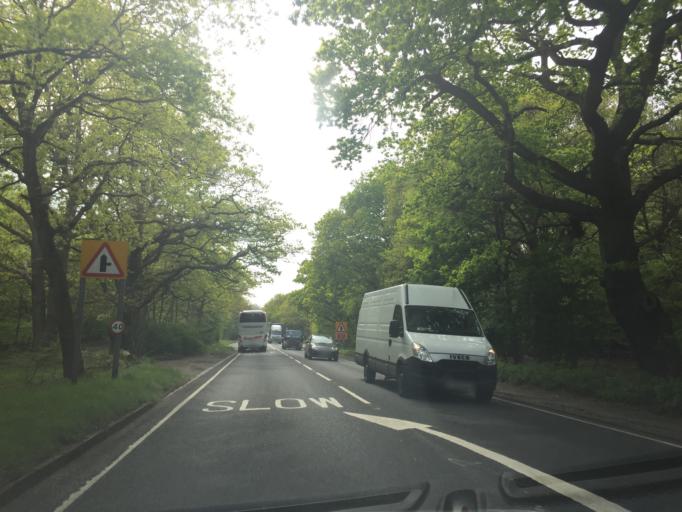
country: GB
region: England
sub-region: Essex
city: Theydon Bois
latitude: 51.6840
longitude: 0.0773
